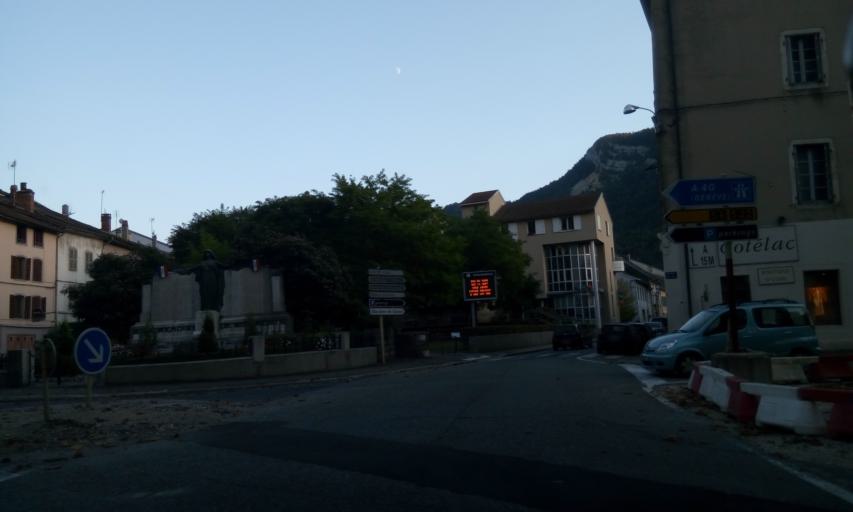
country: FR
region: Rhone-Alpes
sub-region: Departement de l'Ain
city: Nantua
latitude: 46.1567
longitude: 5.6046
